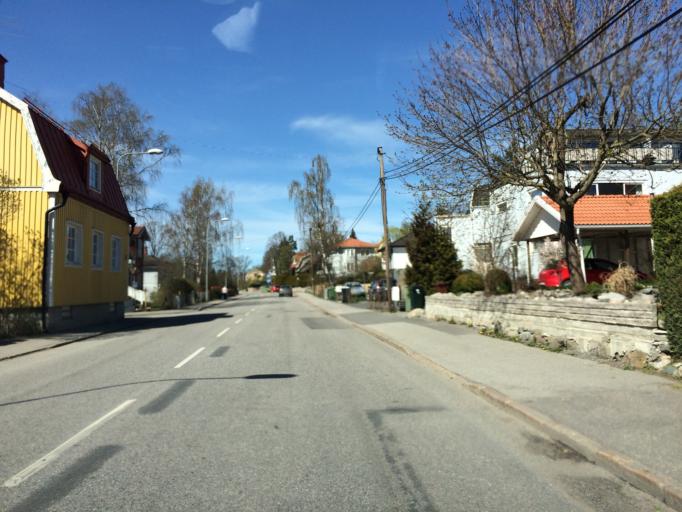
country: SE
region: Stockholm
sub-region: Huddinge Kommun
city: Segeltorp
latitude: 59.2731
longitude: 17.9661
